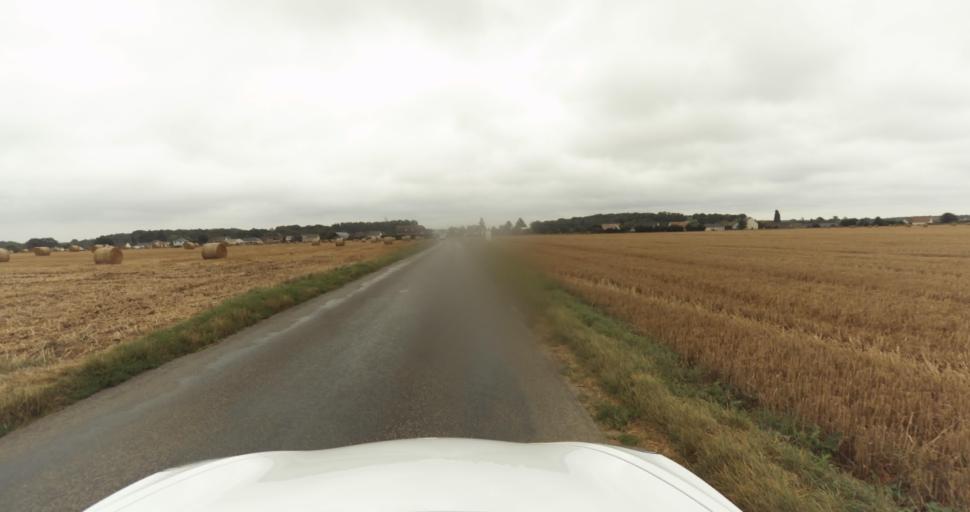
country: FR
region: Haute-Normandie
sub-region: Departement de l'Eure
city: Aviron
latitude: 49.0642
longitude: 1.1223
